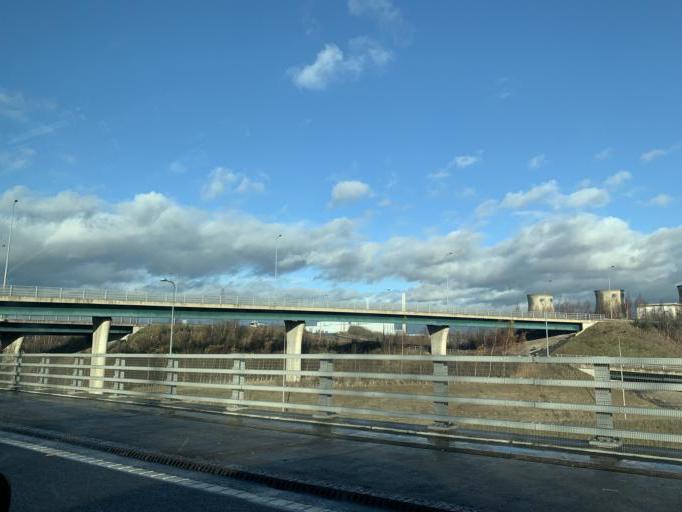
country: GB
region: England
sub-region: City and Borough of Wakefield
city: Ferrybridge
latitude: 53.7109
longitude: -1.2899
